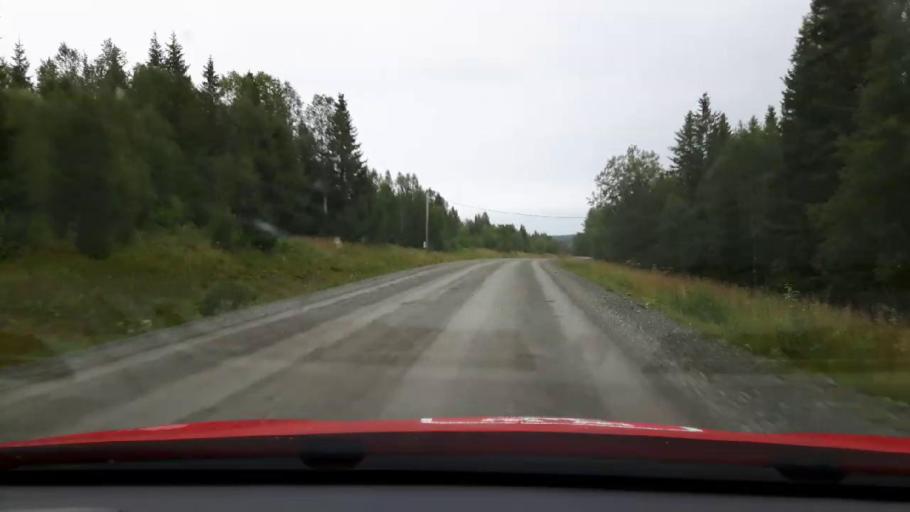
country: SE
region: Jaemtland
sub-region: Are Kommun
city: Are
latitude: 63.4573
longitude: 12.6411
